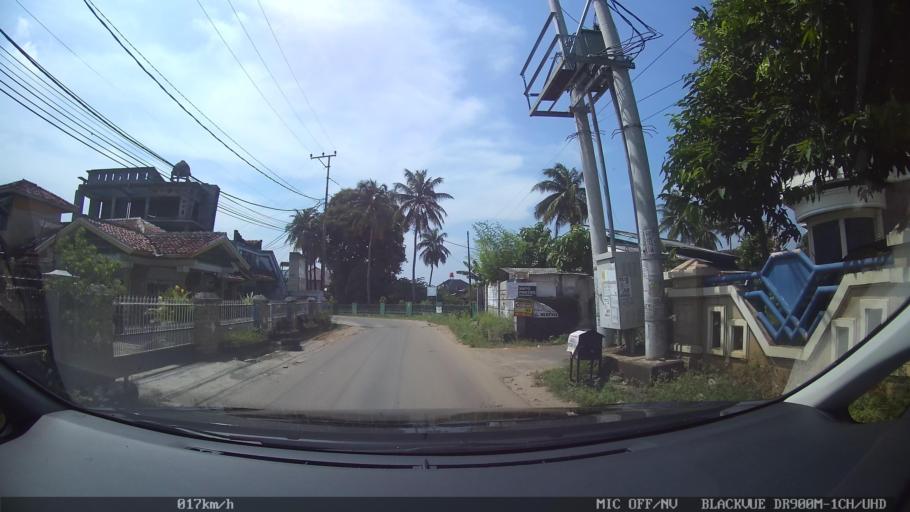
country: ID
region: Lampung
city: Kedaton
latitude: -5.3779
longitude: 105.2605
